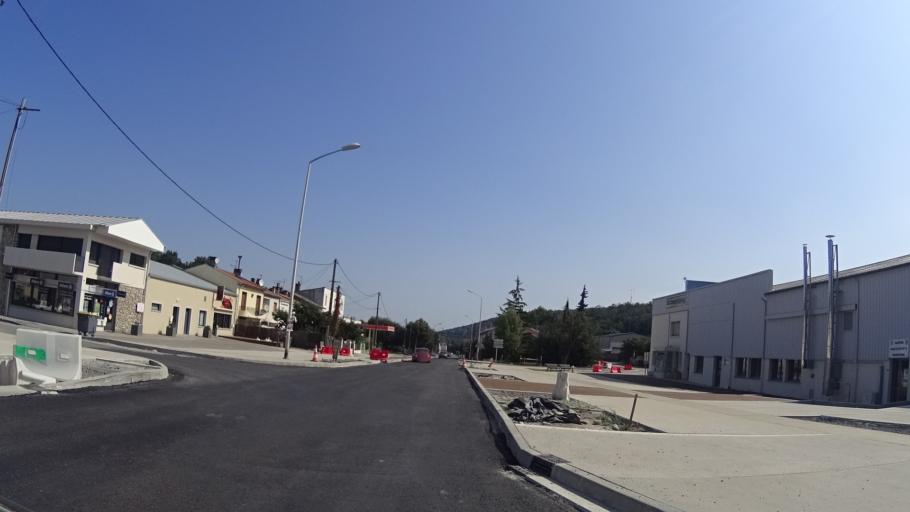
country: FR
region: Midi-Pyrenees
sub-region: Departement de l'Ariege
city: Lavelanet
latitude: 42.9399
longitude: 1.8542
